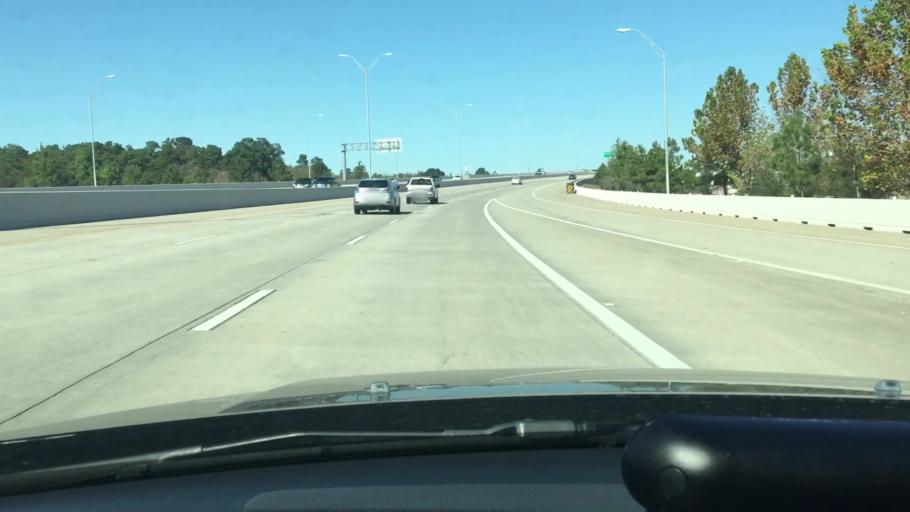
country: US
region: Texas
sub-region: Harris County
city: Sheldon
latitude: 29.8874
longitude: -95.2012
